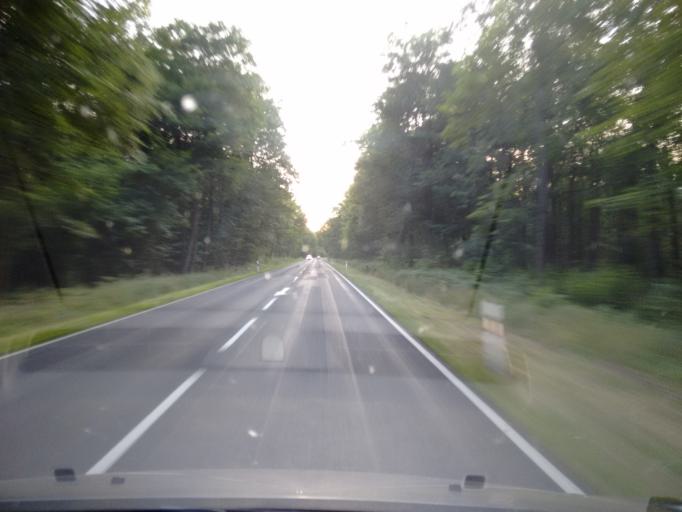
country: DE
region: Brandenburg
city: Mixdorf
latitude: 52.1347
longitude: 14.4413
